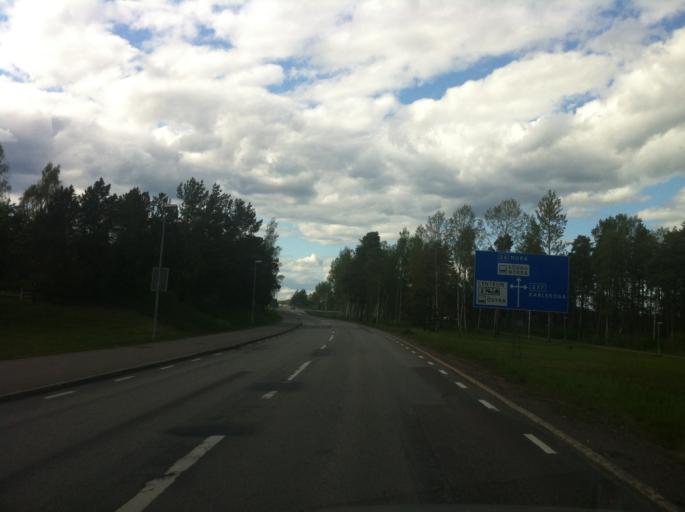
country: SE
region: Vaermland
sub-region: Storfors Kommun
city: Storfors
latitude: 59.5333
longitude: 14.2836
